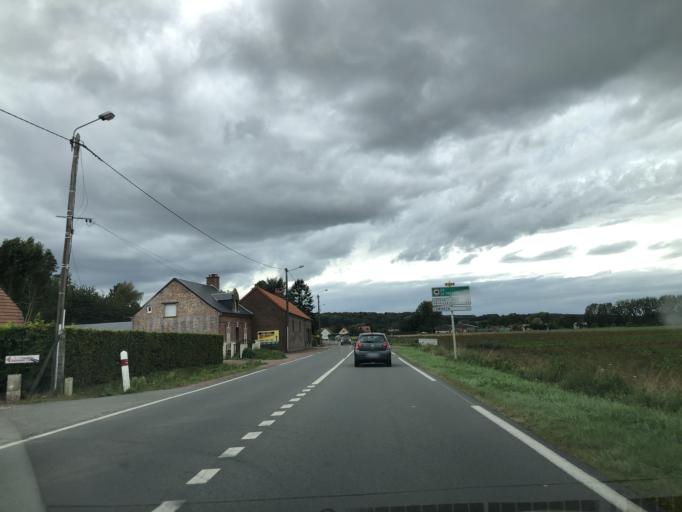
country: FR
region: Picardie
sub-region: Departement de la Somme
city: Abbeville
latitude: 50.1089
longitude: 1.7827
